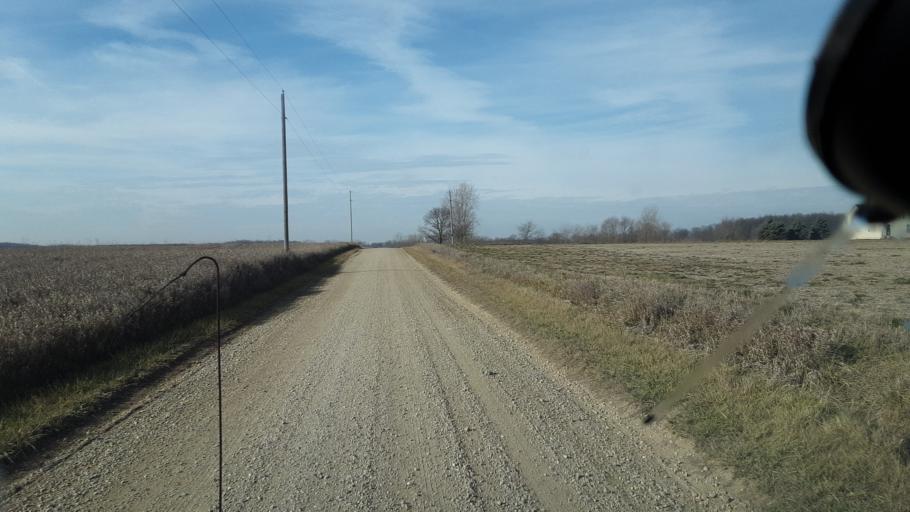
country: US
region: Ohio
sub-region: Defiance County
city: Hicksville
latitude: 41.2708
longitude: -84.8123
